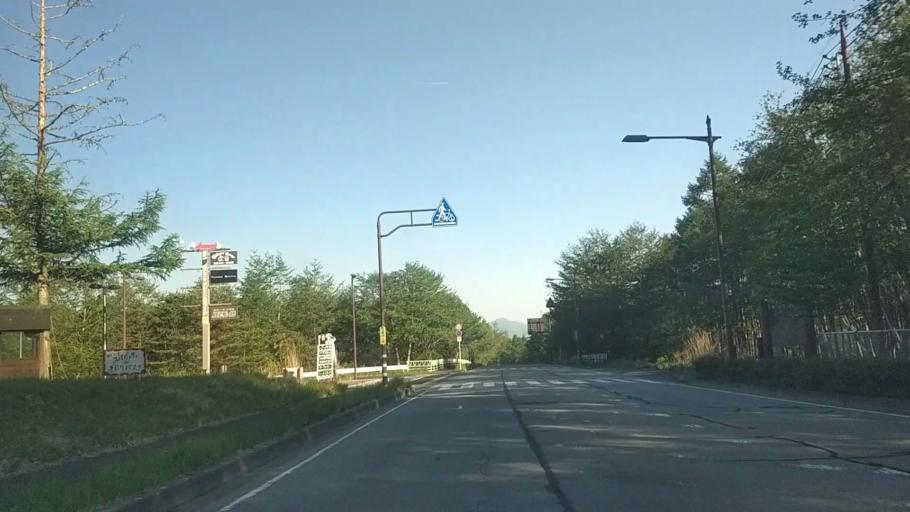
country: JP
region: Yamanashi
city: Nirasaki
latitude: 35.9229
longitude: 138.4336
